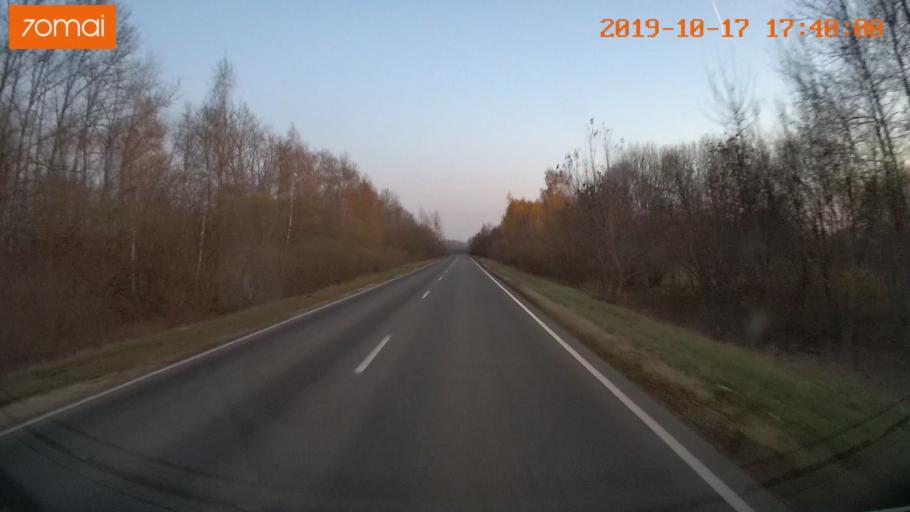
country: RU
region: Tula
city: Yepifan'
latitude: 53.7976
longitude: 38.6006
